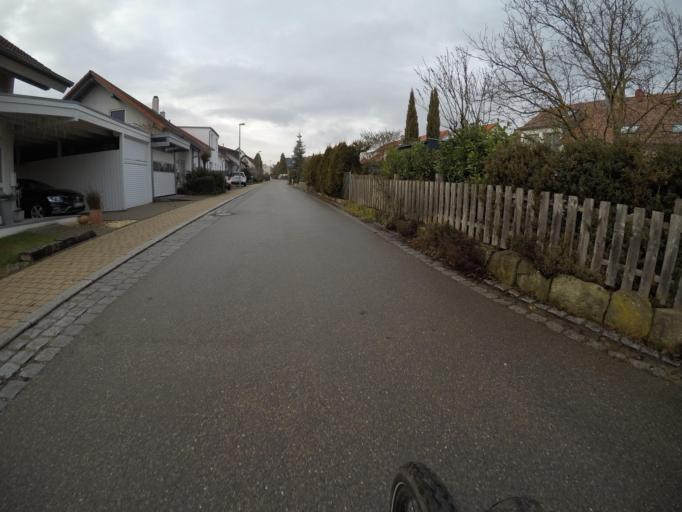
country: DE
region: Baden-Wuerttemberg
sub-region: Regierungsbezirk Stuttgart
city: Filderstadt
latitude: 48.6457
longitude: 9.2484
